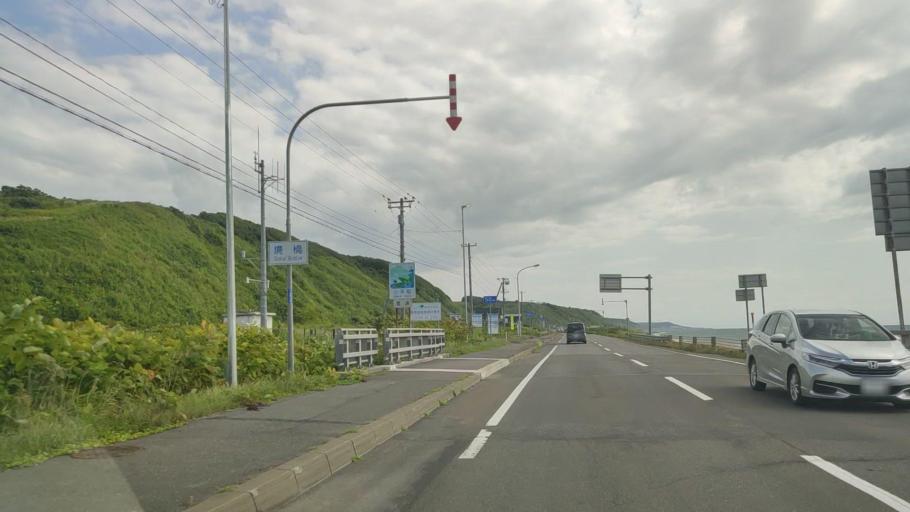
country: JP
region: Hokkaido
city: Rumoi
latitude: 44.2087
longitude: 141.6569
